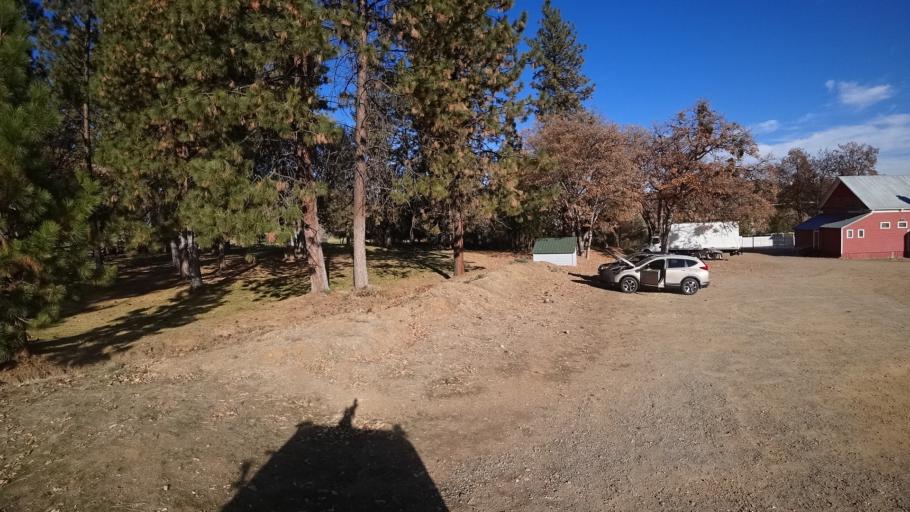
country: US
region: California
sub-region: Siskiyou County
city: Yreka
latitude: 41.7088
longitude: -122.6490
